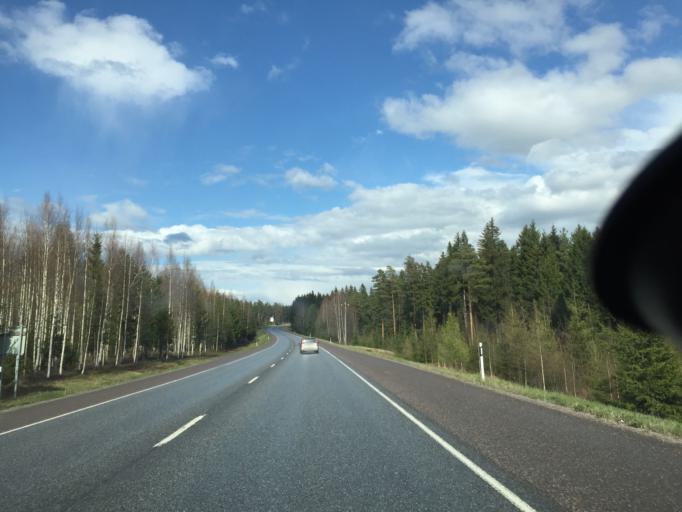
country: FI
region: Uusimaa
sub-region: Raaseporin
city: Karis
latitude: 60.0986
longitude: 23.7686
